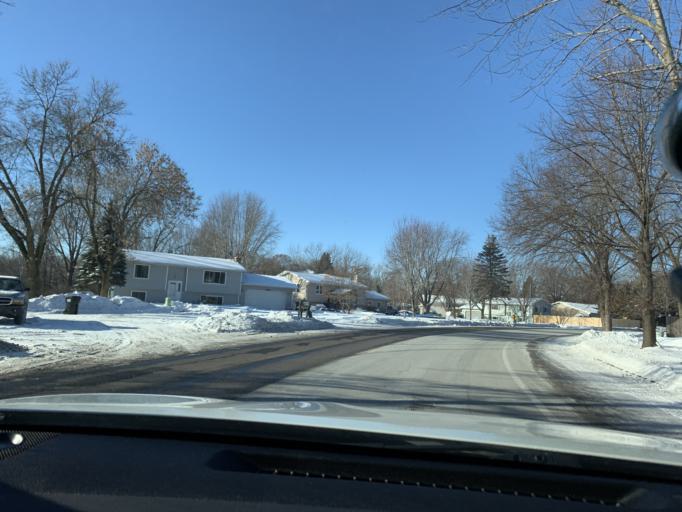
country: US
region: Minnesota
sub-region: Hennepin County
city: West Coon Rapids
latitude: 45.1673
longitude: -93.3025
